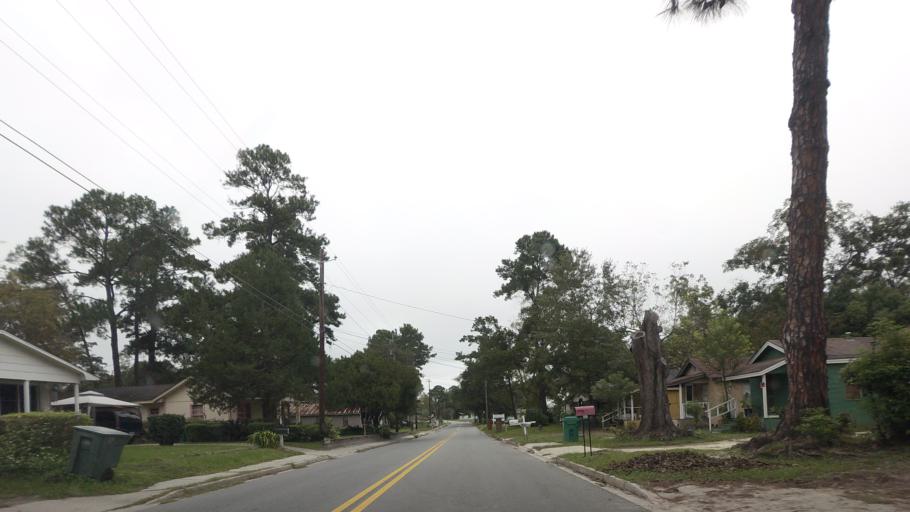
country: US
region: Georgia
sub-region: Lowndes County
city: Valdosta
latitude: 30.8221
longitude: -83.2785
